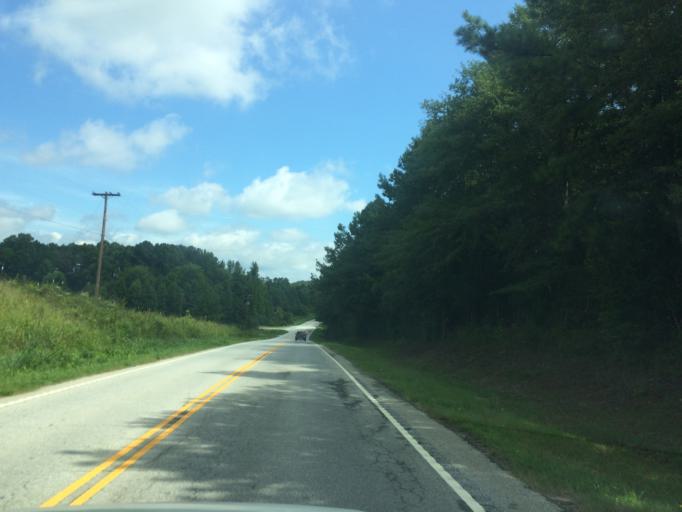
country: US
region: South Carolina
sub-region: Spartanburg County
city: Inman
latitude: 35.0662
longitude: -82.0789
